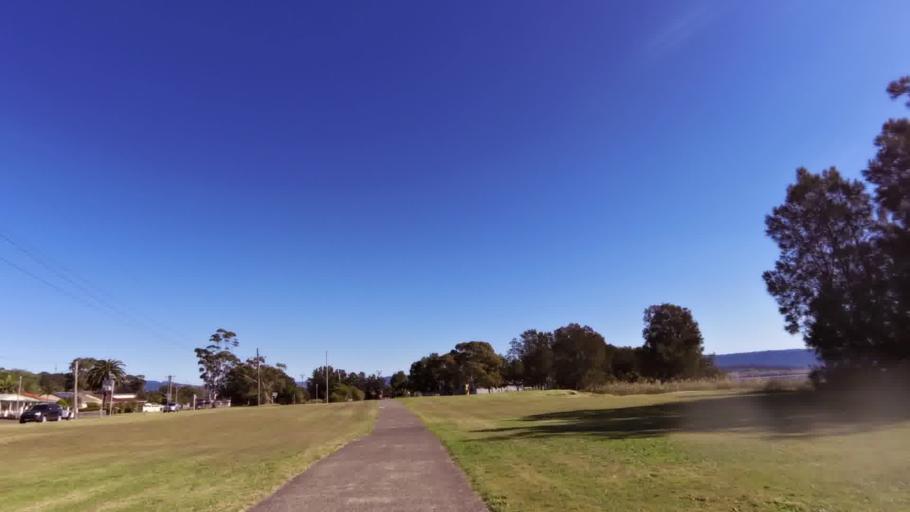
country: AU
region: New South Wales
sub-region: Shellharbour
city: Lake Illawarra
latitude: -34.5388
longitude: 150.8560
